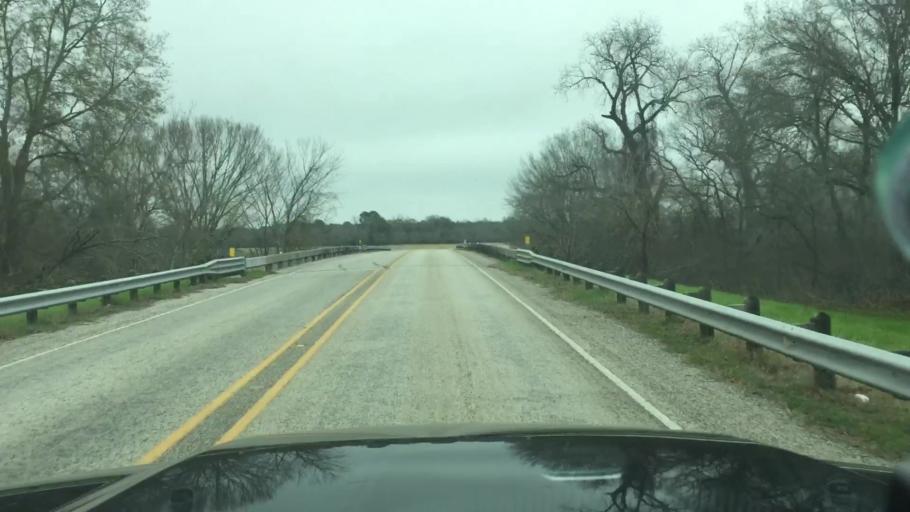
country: US
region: Texas
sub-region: Fayette County
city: La Grange
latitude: 30.0114
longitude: -96.9167
